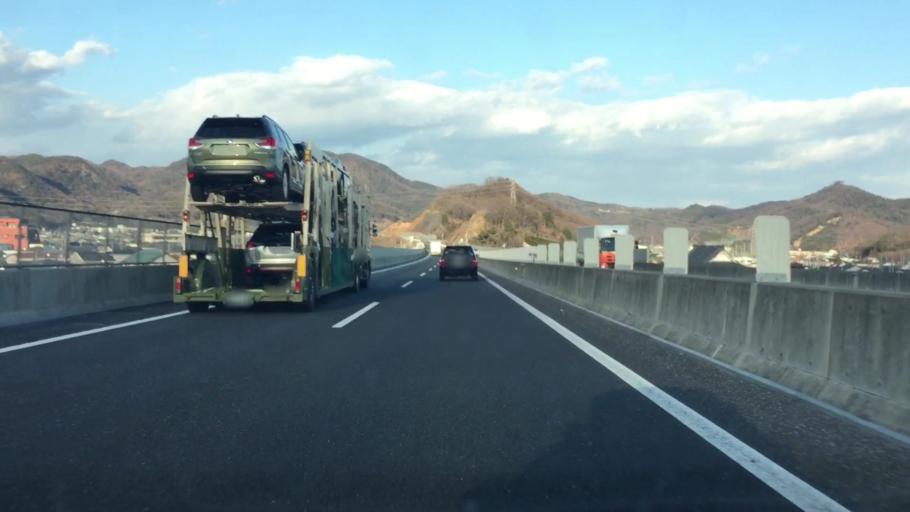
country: JP
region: Tochigi
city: Ashikaga
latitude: 36.3418
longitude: 139.4119
